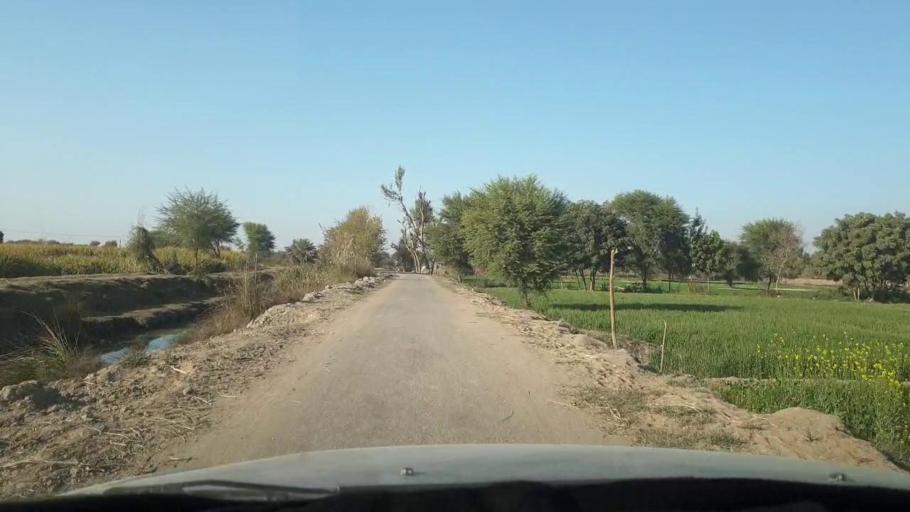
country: PK
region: Sindh
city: Adilpur
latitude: 27.9351
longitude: 69.2605
